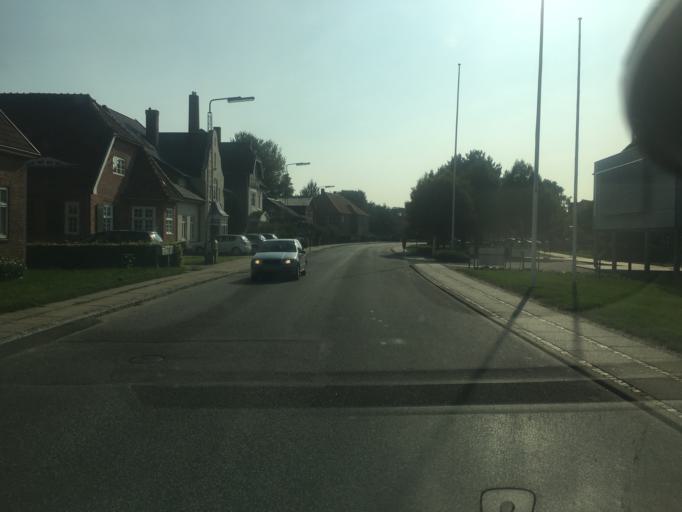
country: DK
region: South Denmark
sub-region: Tonder Kommune
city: Tonder
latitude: 54.9409
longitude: 8.8766
